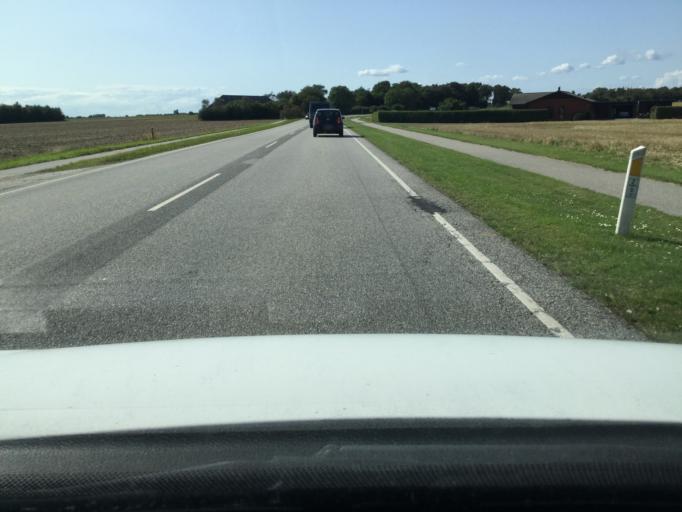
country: DK
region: Zealand
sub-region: Lolland Kommune
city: Nakskov
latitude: 54.8135
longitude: 11.1671
